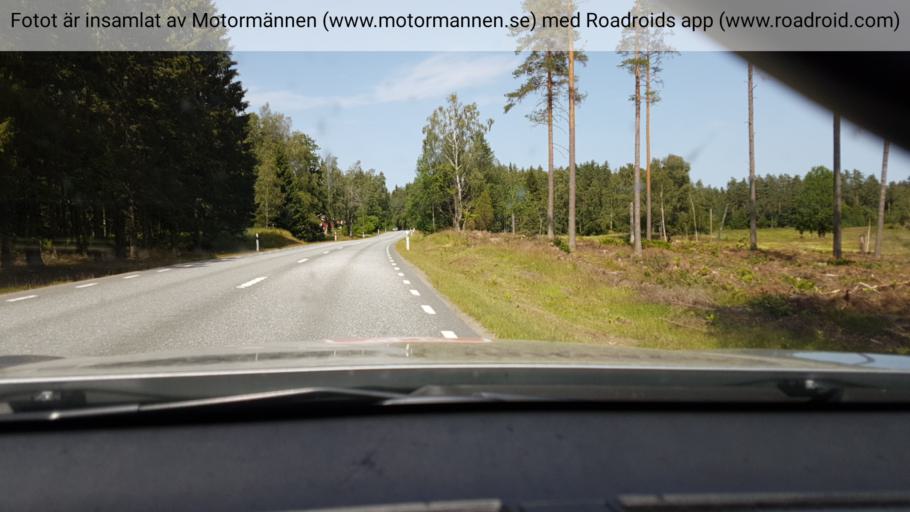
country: SE
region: Joenkoeping
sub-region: Nassjo Kommun
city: Bodafors
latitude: 57.5366
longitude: 14.7880
